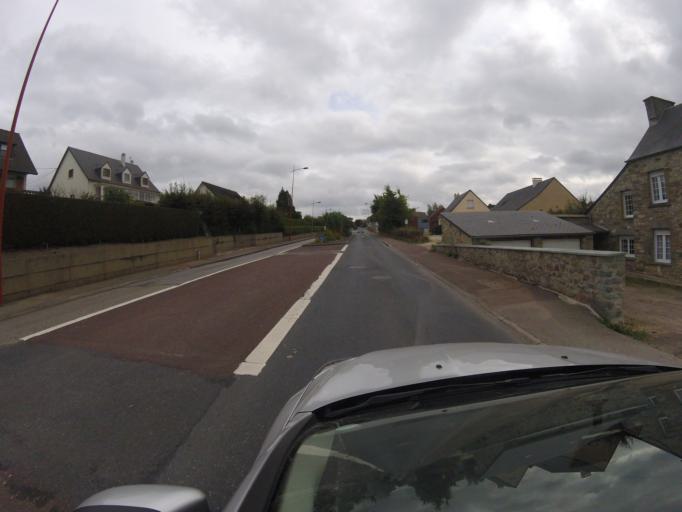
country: FR
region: Lower Normandy
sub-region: Departement de la Manche
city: La Glacerie
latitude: 49.6153
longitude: -1.6053
